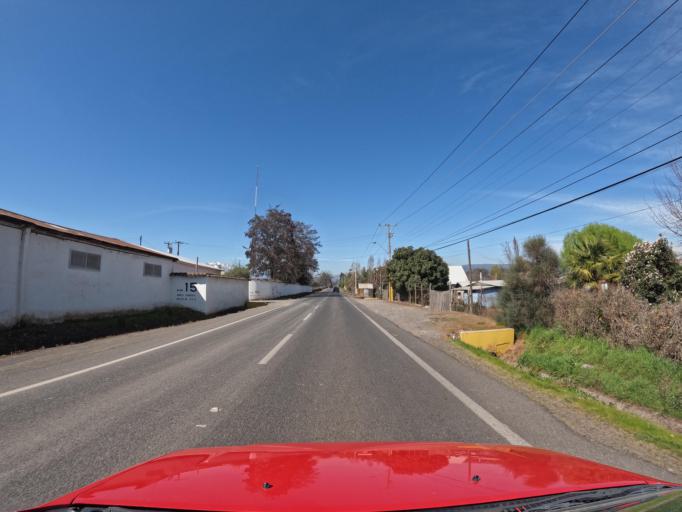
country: CL
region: Maule
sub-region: Provincia de Curico
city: Teno
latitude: -34.9675
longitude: -71.0307
